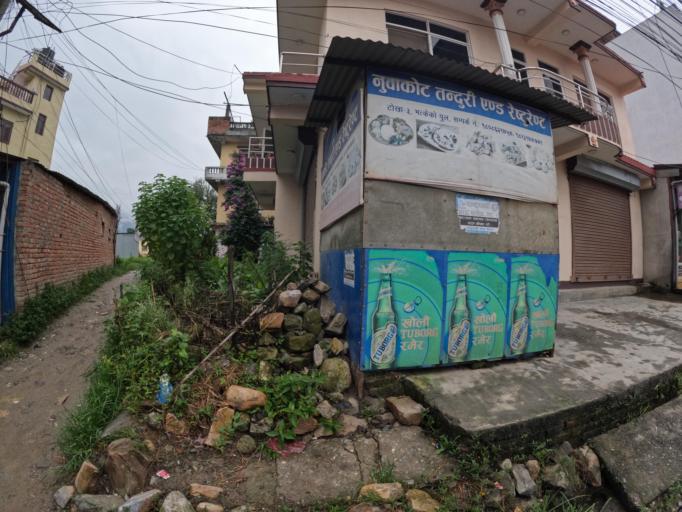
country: NP
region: Central Region
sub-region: Bagmati Zone
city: Kathmandu
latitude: 27.7617
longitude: 85.3190
